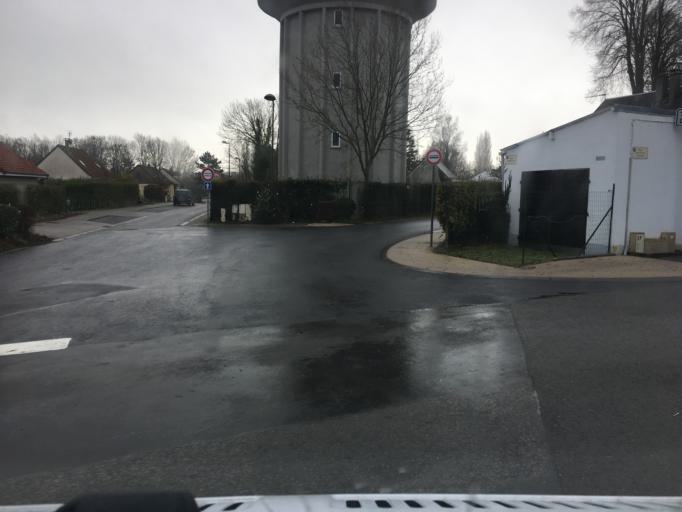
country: FR
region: Picardie
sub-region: Departement de la Somme
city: Saint-Valery-sur-Somme
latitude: 50.1809
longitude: 1.6315
